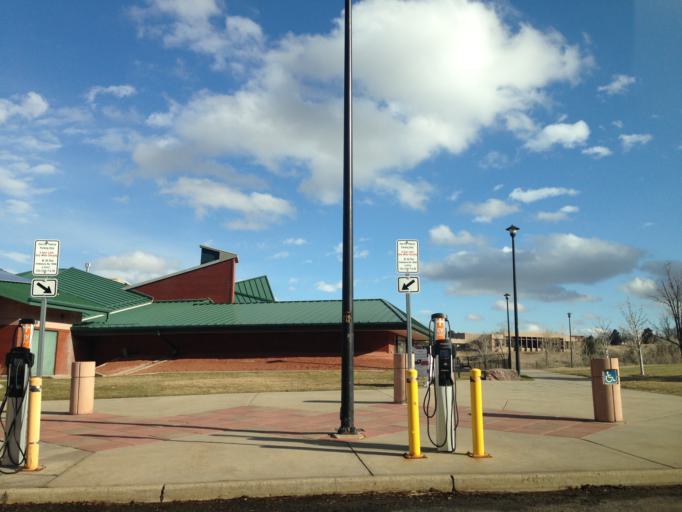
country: US
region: Colorado
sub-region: Boulder County
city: Boulder
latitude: 39.9748
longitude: -105.2493
